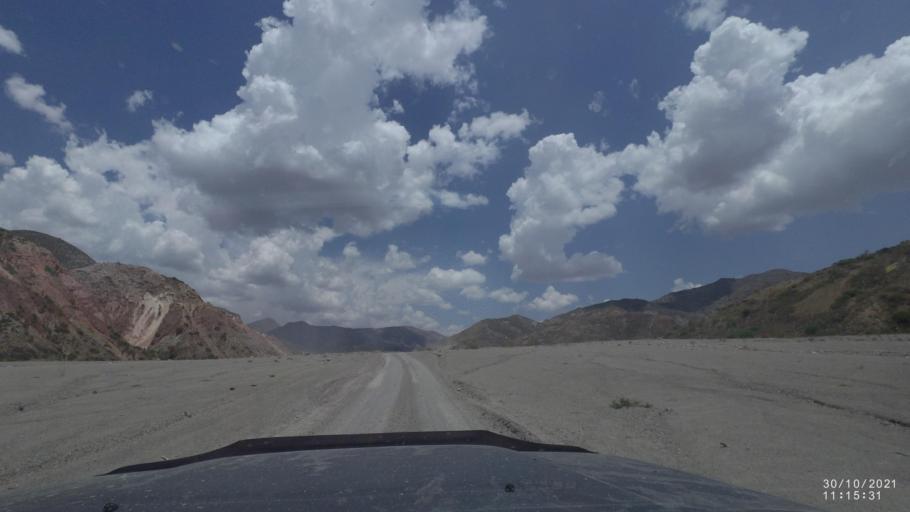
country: BO
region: Cochabamba
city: Sipe Sipe
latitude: -17.5249
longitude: -66.5896
